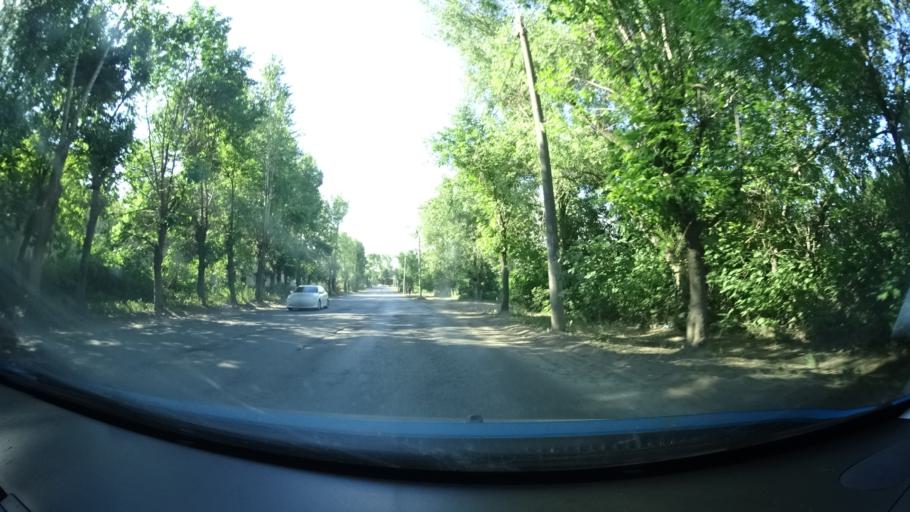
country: RU
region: Bashkortostan
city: Ufa
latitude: 54.8381
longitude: 56.0757
